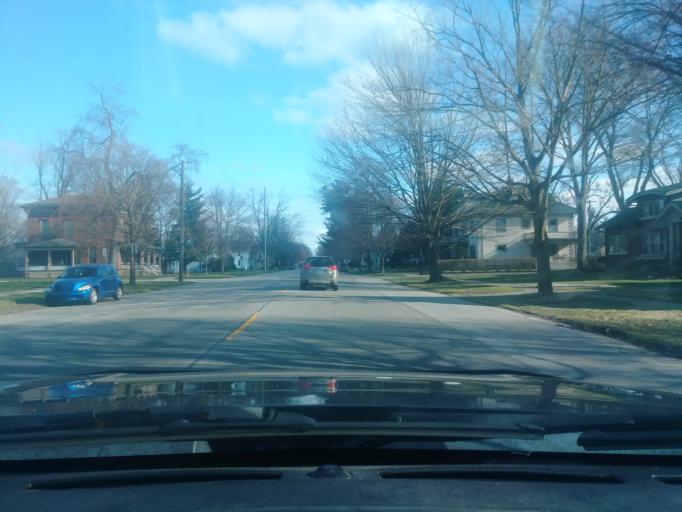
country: US
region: Indiana
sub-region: LaPorte County
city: LaPorte
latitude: 41.6055
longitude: -86.7176
